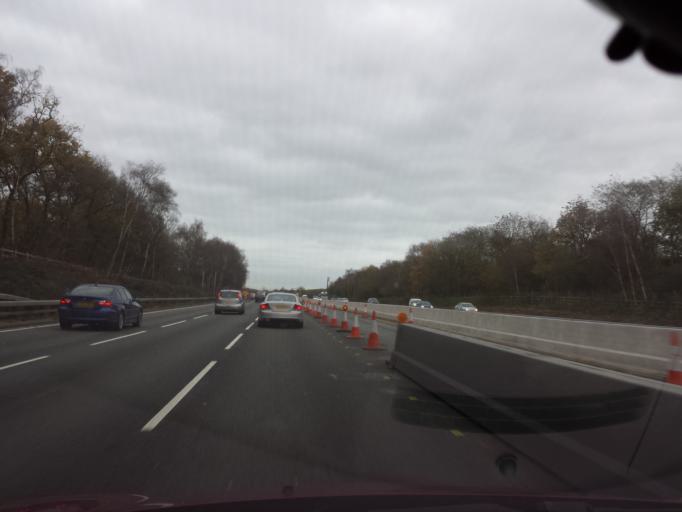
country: GB
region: England
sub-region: Surrey
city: Virginia Water
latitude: 51.3892
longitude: -0.5705
